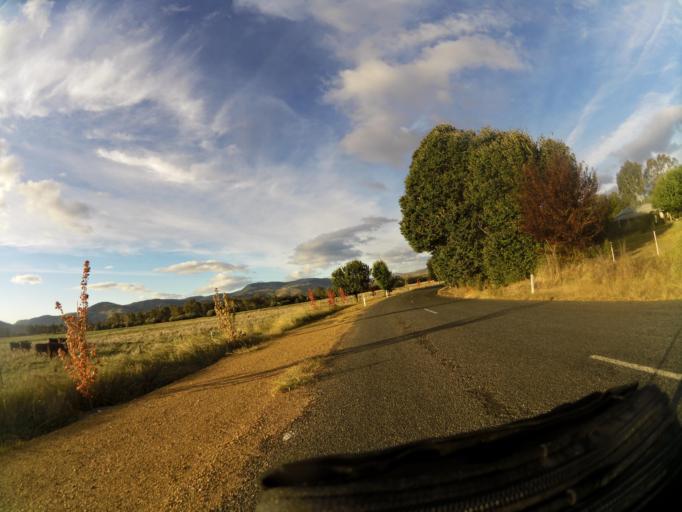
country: AU
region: New South Wales
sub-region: Greater Hume Shire
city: Holbrook
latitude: -36.0475
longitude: 147.9259
